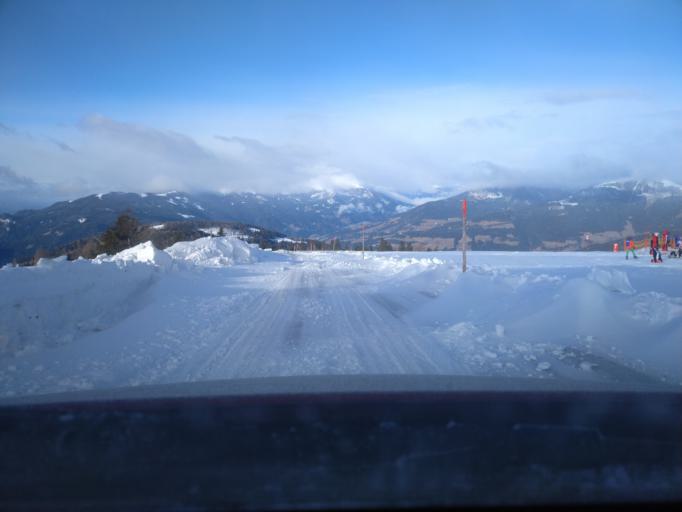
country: AT
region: Carinthia
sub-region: Politischer Bezirk Villach Land
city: Arriach
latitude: 46.6966
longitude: 13.9104
